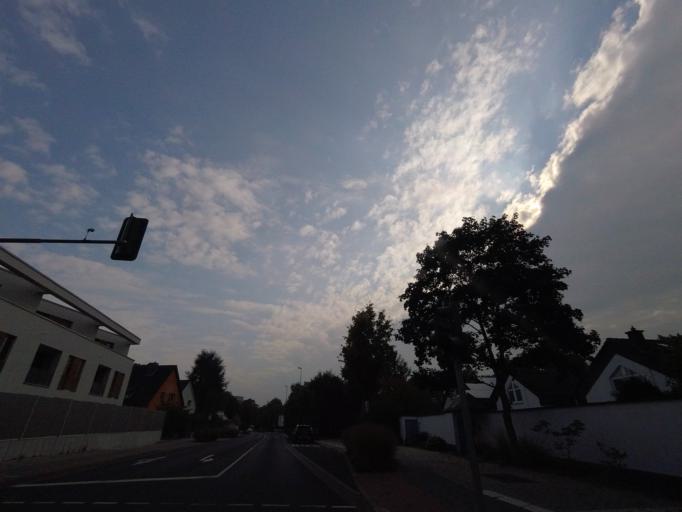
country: DE
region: Hesse
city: Liederbach
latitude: 50.1169
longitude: 8.4955
